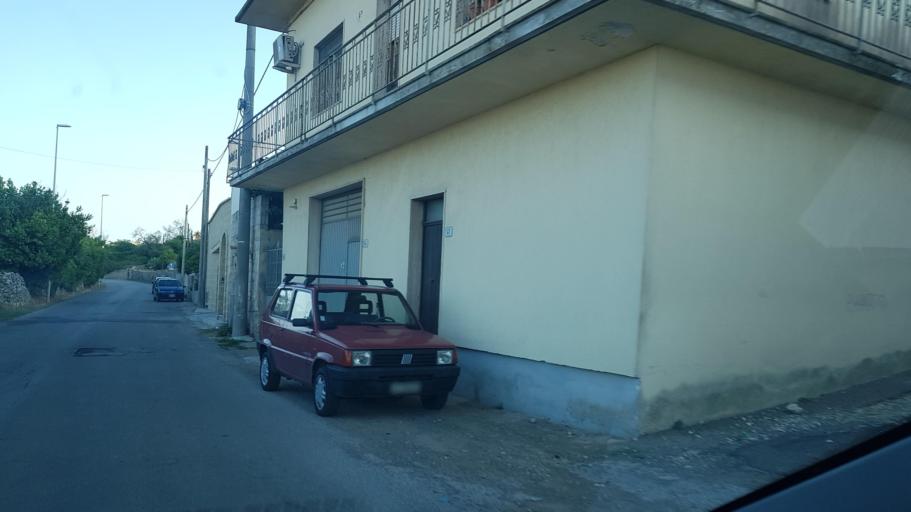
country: IT
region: Apulia
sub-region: Provincia di Lecce
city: Specchia
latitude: 39.9414
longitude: 18.3017
